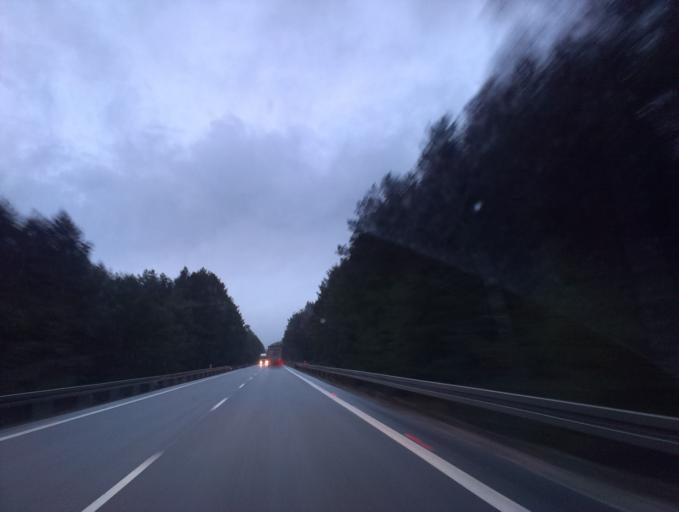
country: PL
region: Swietokrzyskie
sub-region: Powiat konecki
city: Ruda Maleniecka
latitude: 51.1920
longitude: 20.2122
